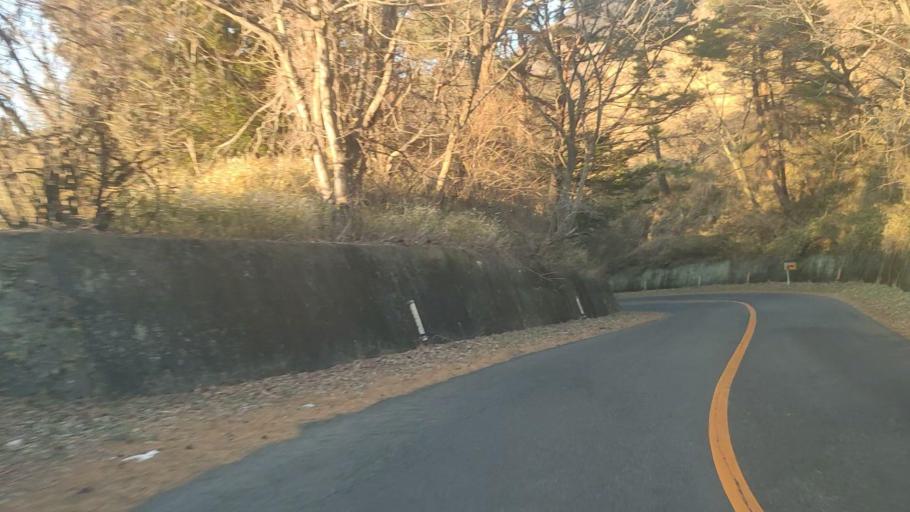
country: JP
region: Oita
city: Beppu
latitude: 33.2594
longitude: 131.3784
